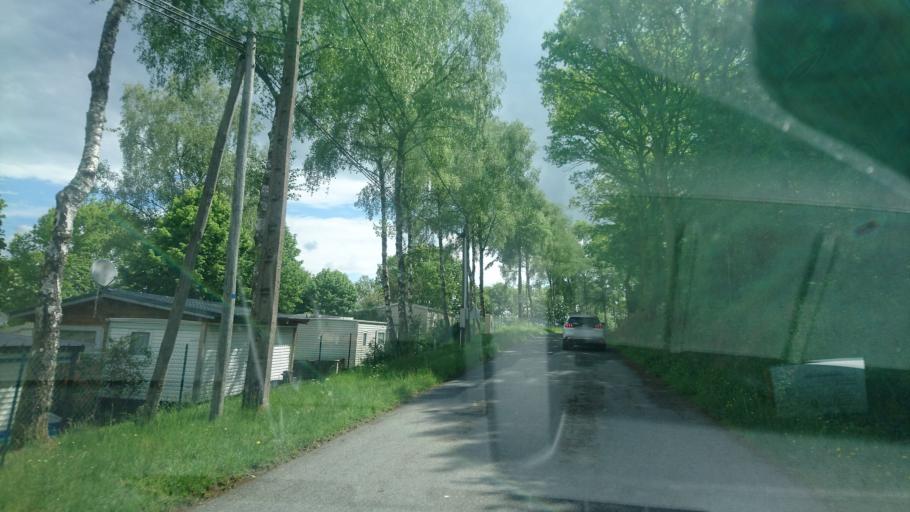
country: FR
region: Limousin
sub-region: Departement de la Haute-Vienne
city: Peyrat-le-Chateau
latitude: 45.7889
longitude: 1.8965
